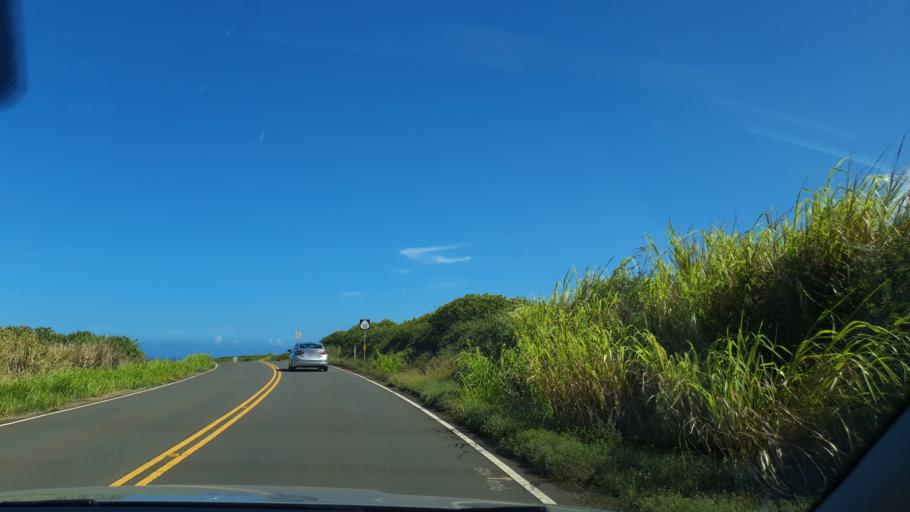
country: US
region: Hawaii
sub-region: Maui County
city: Napili-Honokowai
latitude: 21.0144
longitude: -156.5735
